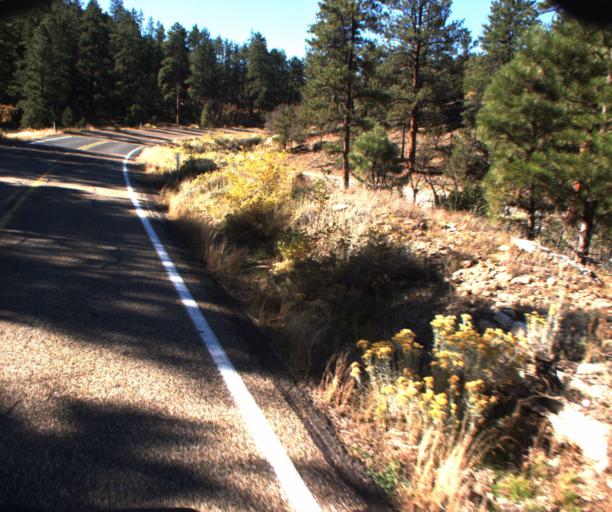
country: US
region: Arizona
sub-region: Coconino County
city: Fredonia
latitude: 36.7396
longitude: -112.1252
